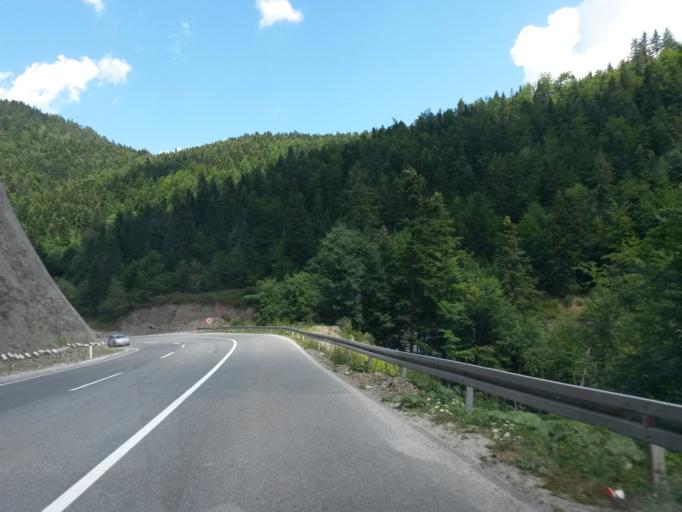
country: BA
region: Federation of Bosnia and Herzegovina
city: Bugojno
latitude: 44.0307
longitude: 17.3469
